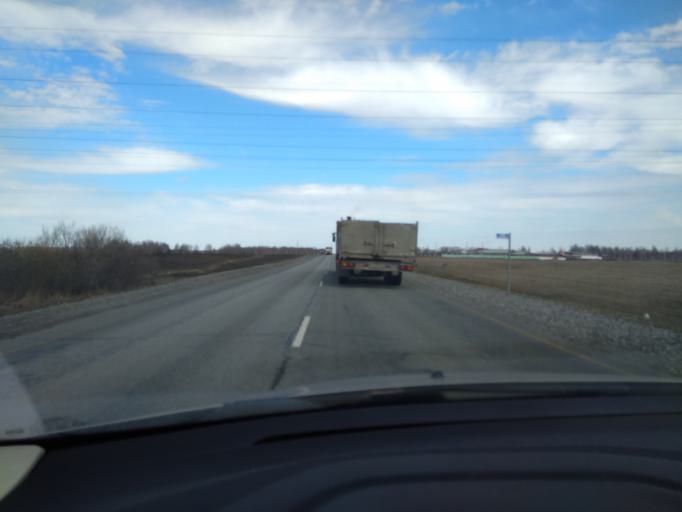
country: RU
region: Sverdlovsk
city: Pyshma
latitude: 56.9806
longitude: 63.2446
